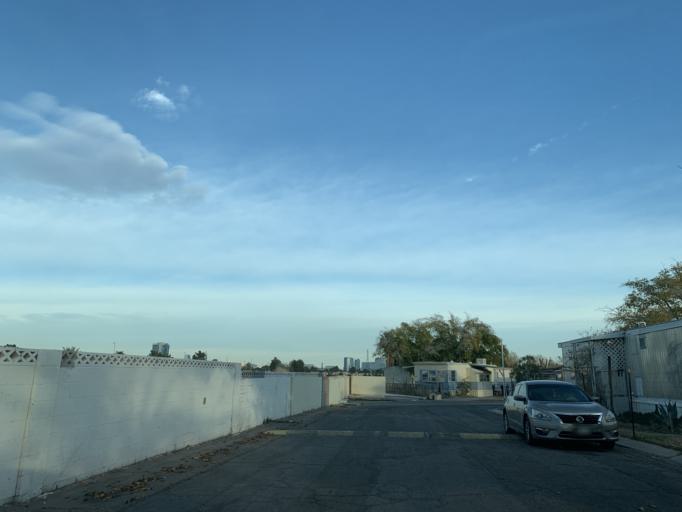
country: US
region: Nevada
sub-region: Clark County
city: Spring Valley
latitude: 36.1036
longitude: -115.2222
